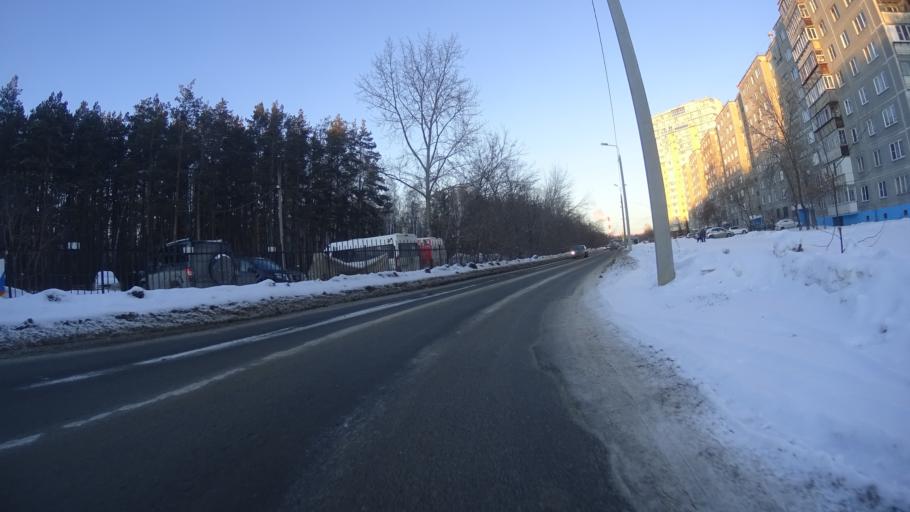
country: RU
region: Chelyabinsk
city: Roshchino
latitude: 55.1966
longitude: 61.2984
